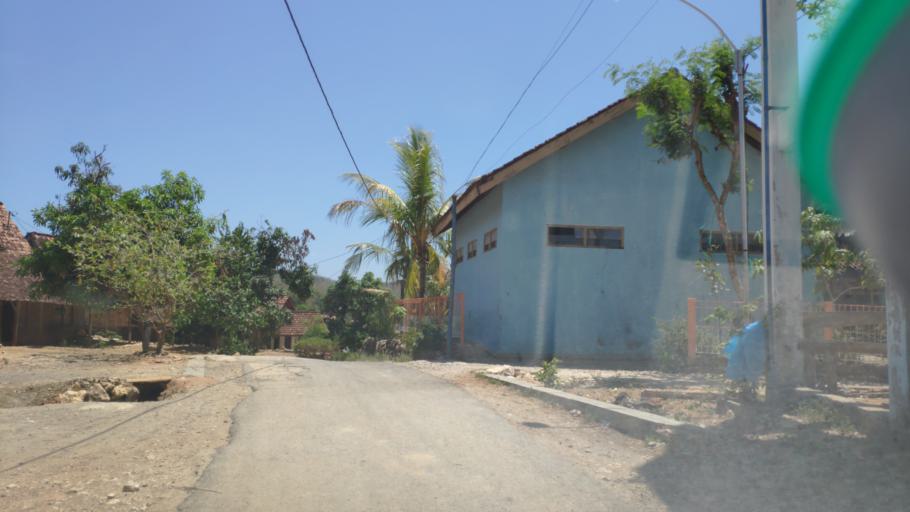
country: ID
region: Central Java
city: Blimbing
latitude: -6.9086
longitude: 111.5464
